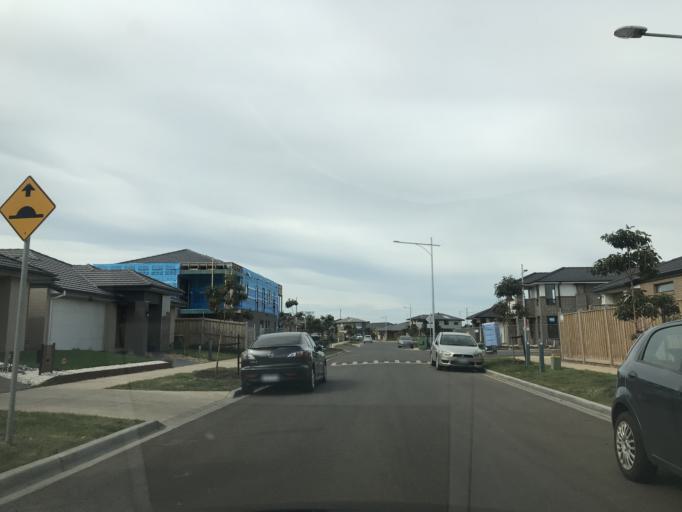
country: AU
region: Victoria
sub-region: Wyndham
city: Truganina
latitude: -37.8332
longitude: 144.7111
